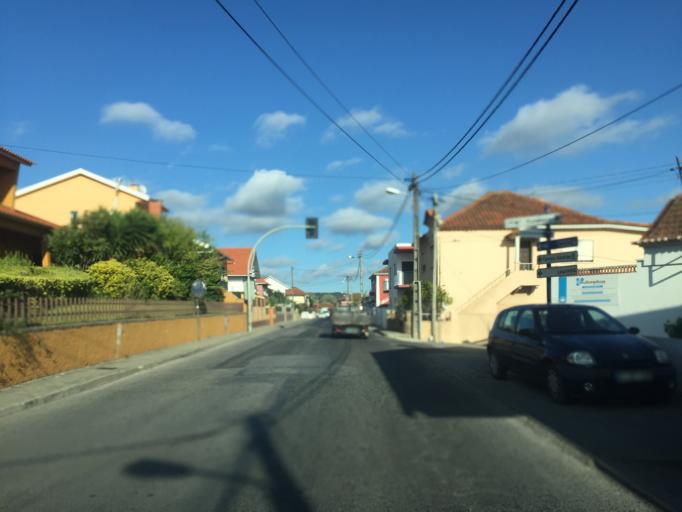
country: PT
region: Lisbon
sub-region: Torres Vedras
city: A dos Cunhados
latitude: 39.1489
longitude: -9.2940
